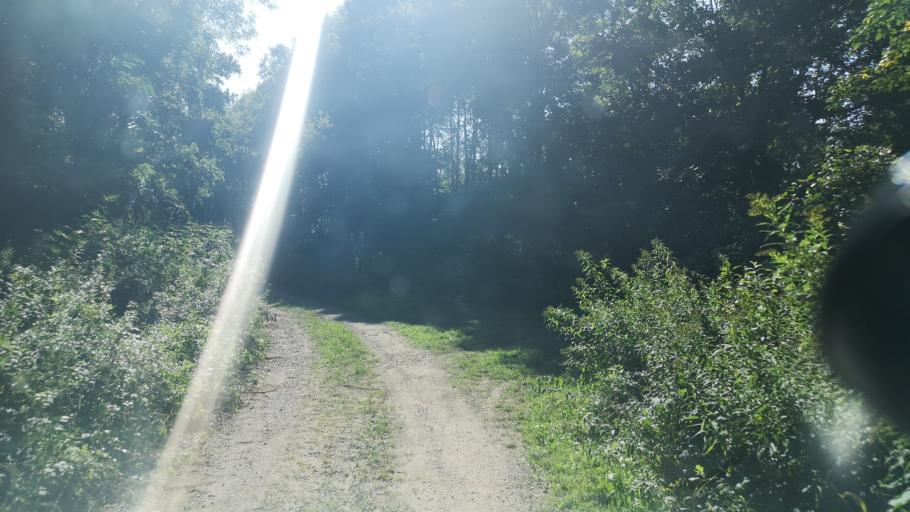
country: SK
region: Trnavsky
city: Smolenice
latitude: 48.5762
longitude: 17.4332
